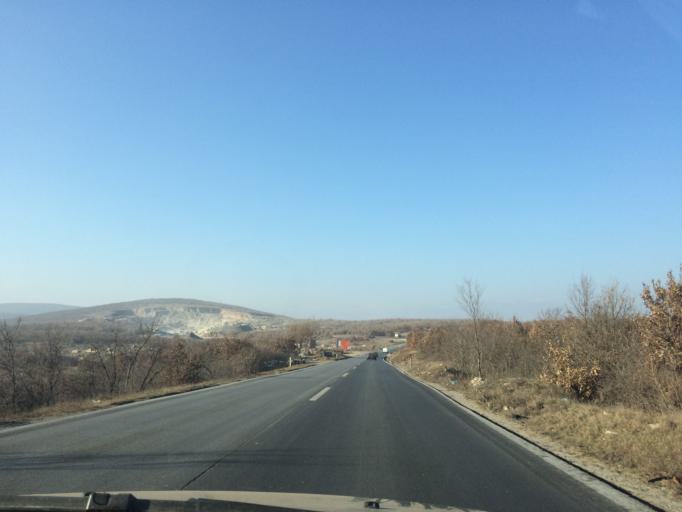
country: XK
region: Pec
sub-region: Komuna e Klines
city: Klina
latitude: 42.5943
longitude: 20.6393
